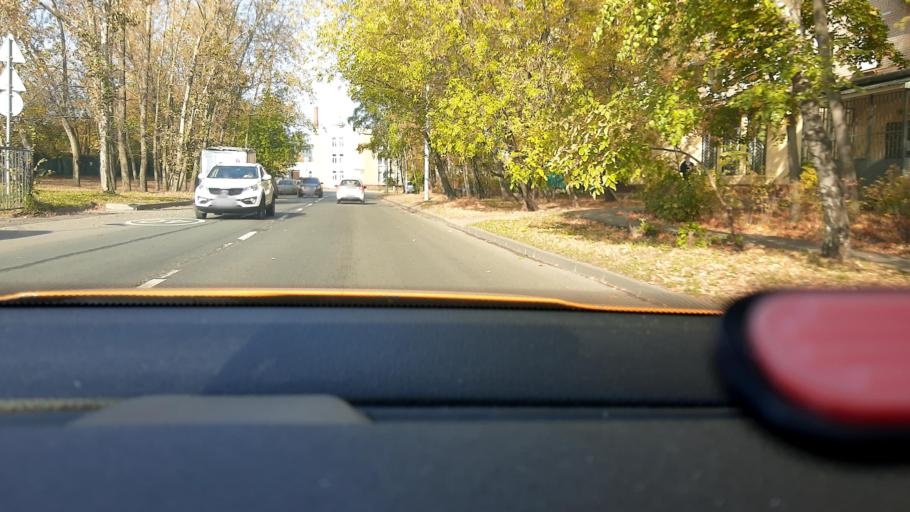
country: RU
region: Moscow
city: Vagonoremont
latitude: 55.8965
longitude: 37.5297
